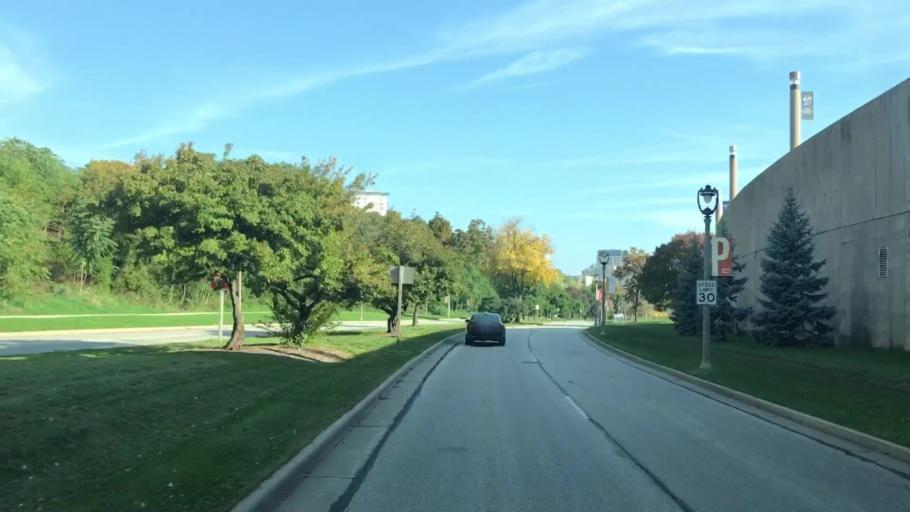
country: US
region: Wisconsin
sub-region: Milwaukee County
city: Milwaukee
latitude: 43.0406
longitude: -87.8982
